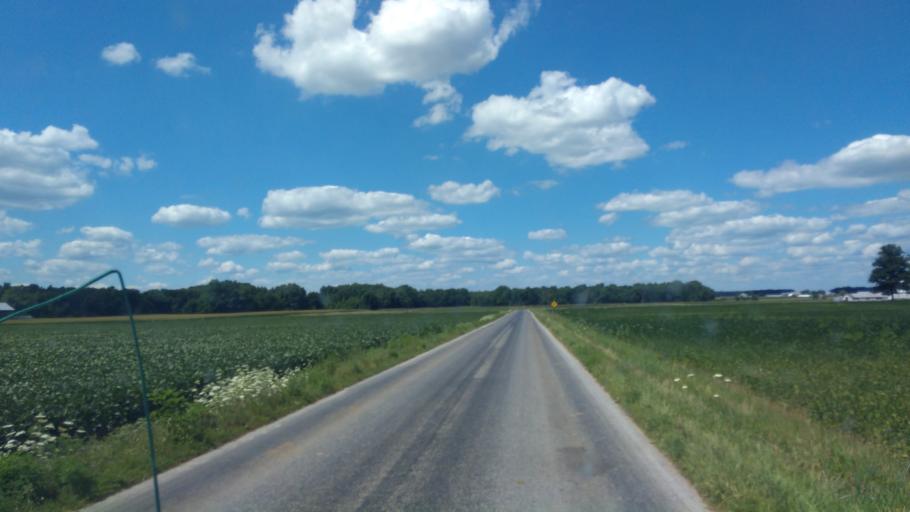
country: US
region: Indiana
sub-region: Adams County
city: Geneva
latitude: 40.5937
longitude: -84.9335
